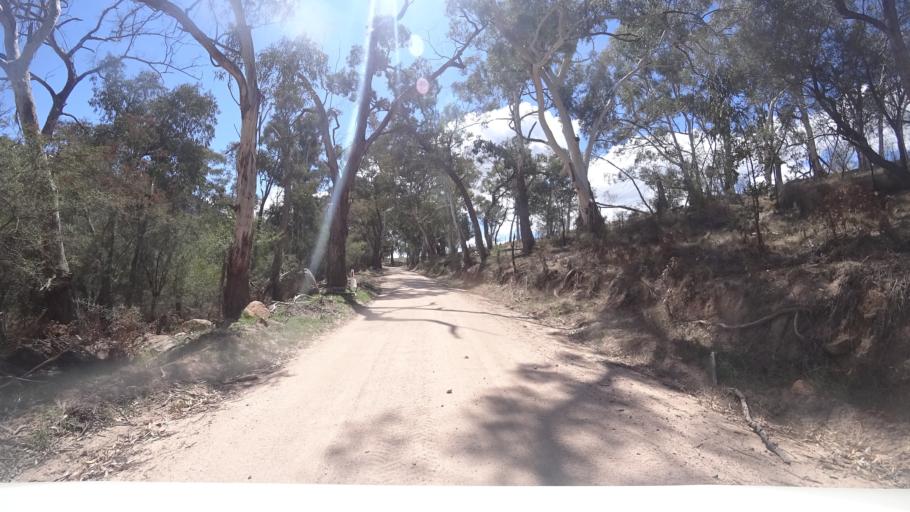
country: AU
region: New South Wales
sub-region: Oberon
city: Oberon
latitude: -33.5423
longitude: 149.9325
